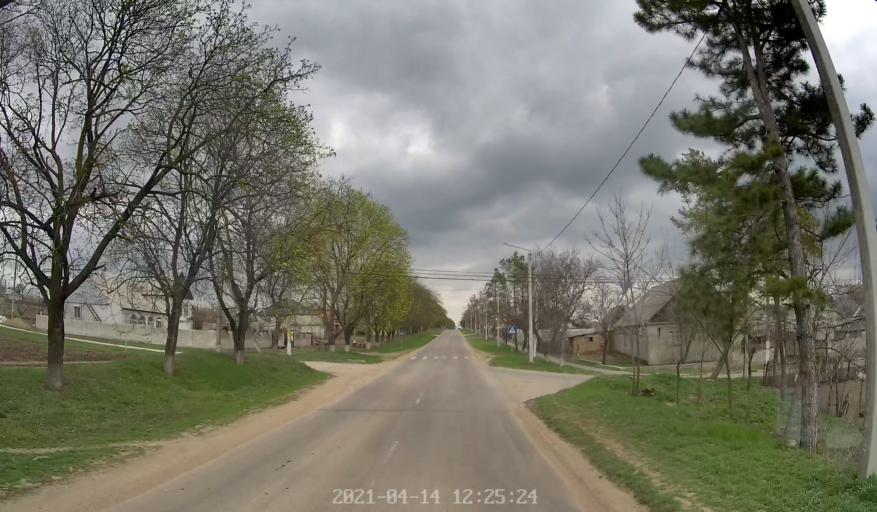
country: MD
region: Criuleni
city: Criuleni
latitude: 47.1744
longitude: 29.1967
